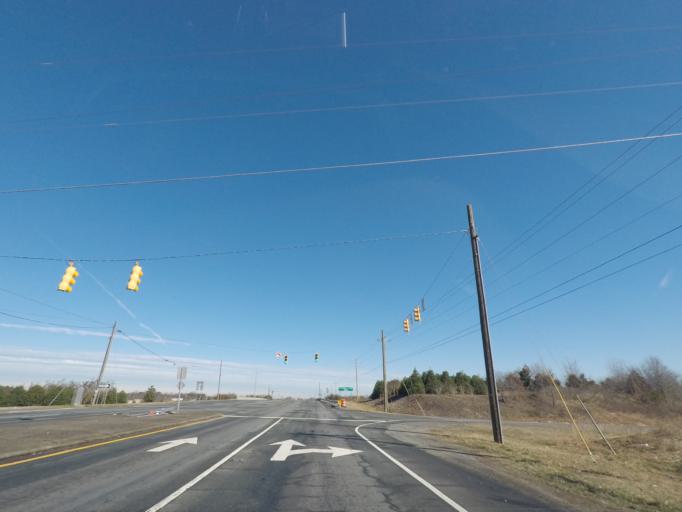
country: US
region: North Carolina
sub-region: Guilford County
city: Pleasant Garden
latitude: 35.9993
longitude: -79.7922
